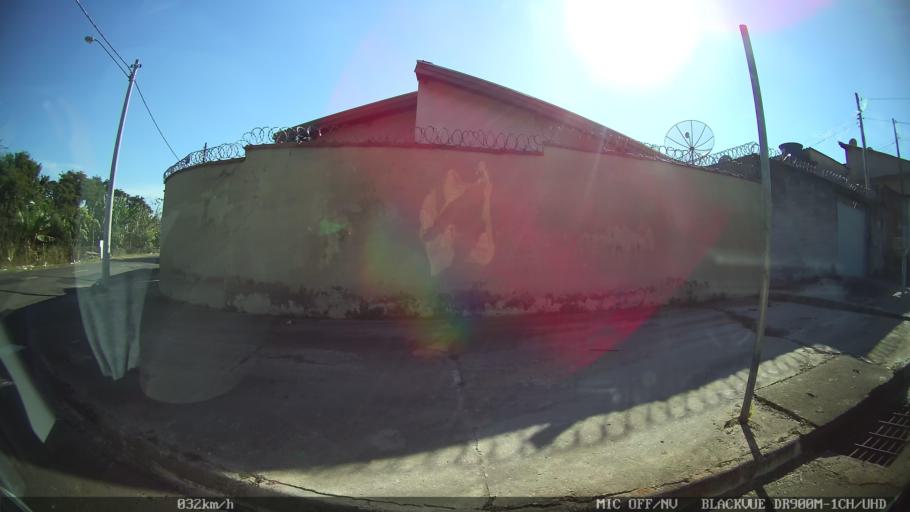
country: BR
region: Sao Paulo
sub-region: Franca
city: Franca
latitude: -20.4912
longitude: -47.4158
